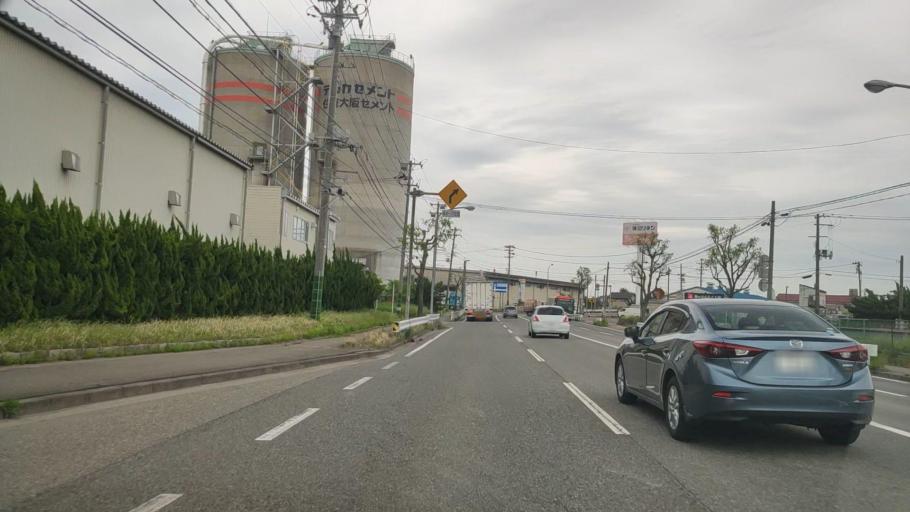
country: JP
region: Niigata
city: Niigata-shi
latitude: 37.9306
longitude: 139.0687
